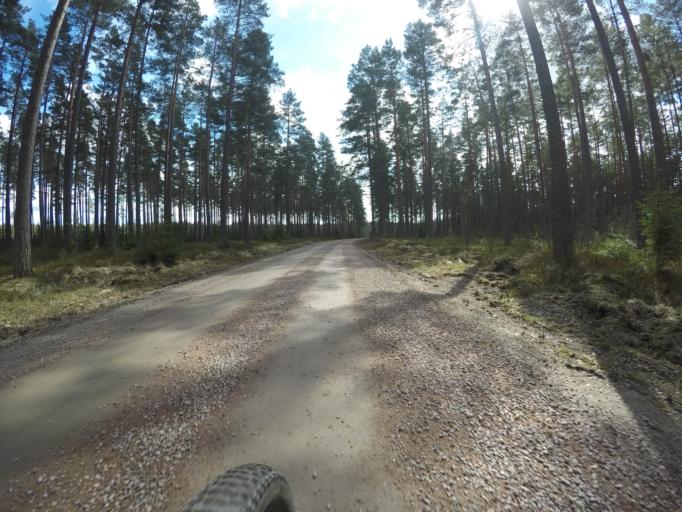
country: SE
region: Vaestmanland
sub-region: Kungsors Kommun
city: Kungsoer
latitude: 59.3702
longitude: 16.1007
